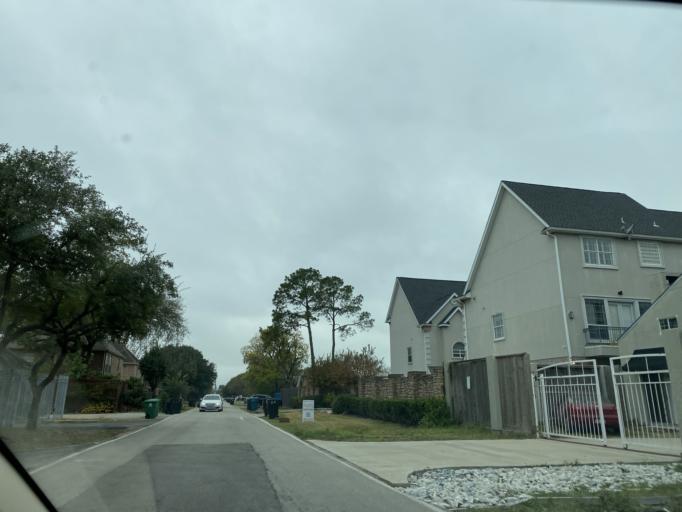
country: US
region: Texas
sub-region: Harris County
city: Bellaire
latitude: 29.7343
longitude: -95.4805
